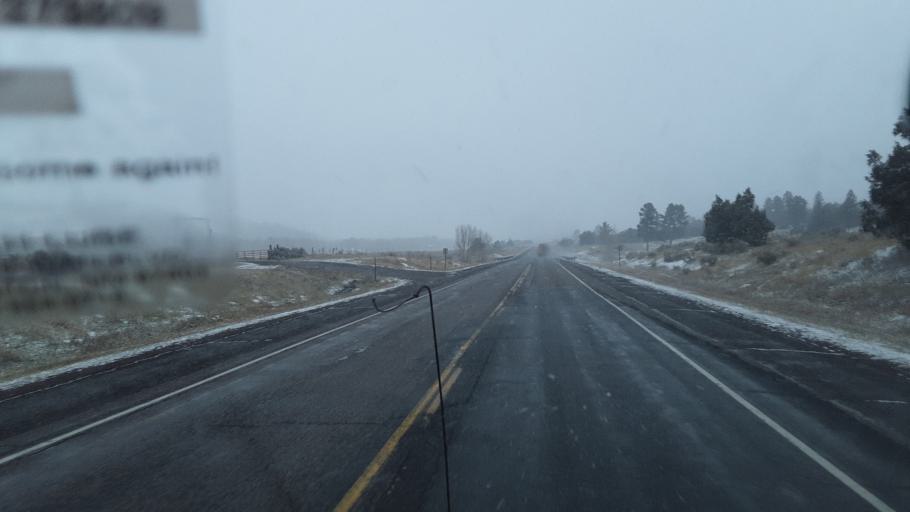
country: US
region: New Mexico
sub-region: Rio Arriba County
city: Chama
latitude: 36.8166
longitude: -106.5688
